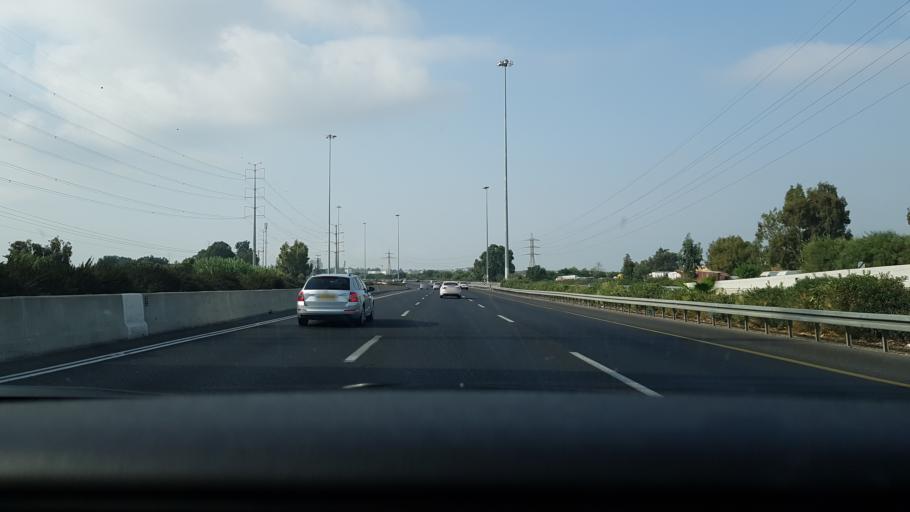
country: IL
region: Central District
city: Bet Dagan
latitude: 31.9999
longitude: 34.8044
